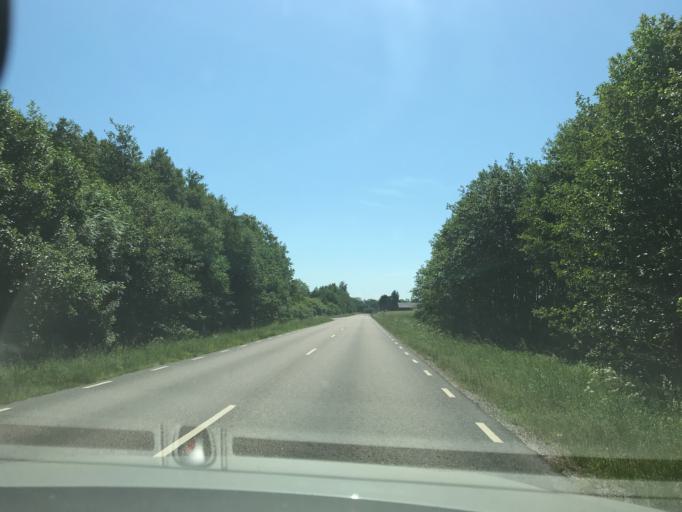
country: SE
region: Vaestra Goetaland
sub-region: Gotene Kommun
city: Kallby
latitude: 58.5889
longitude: 13.3791
